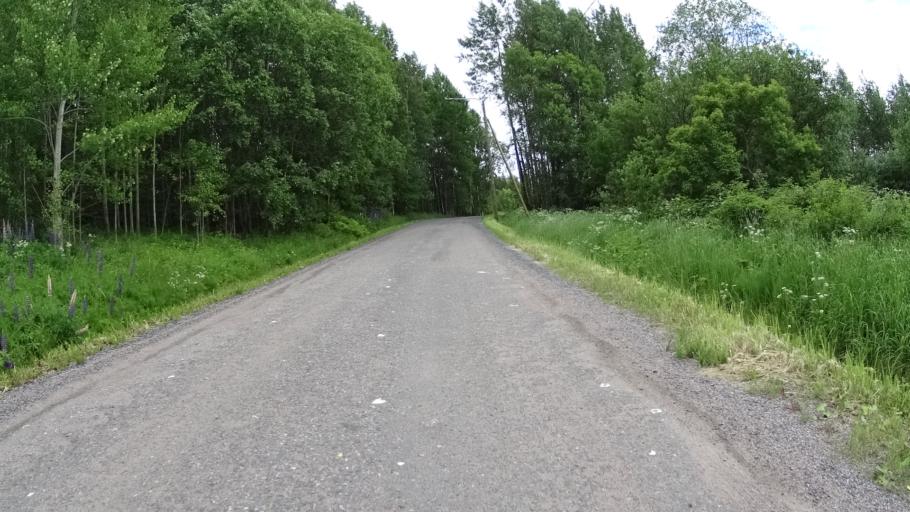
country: FI
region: Uusimaa
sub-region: Helsinki
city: Kilo
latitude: 60.2887
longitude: 24.8237
